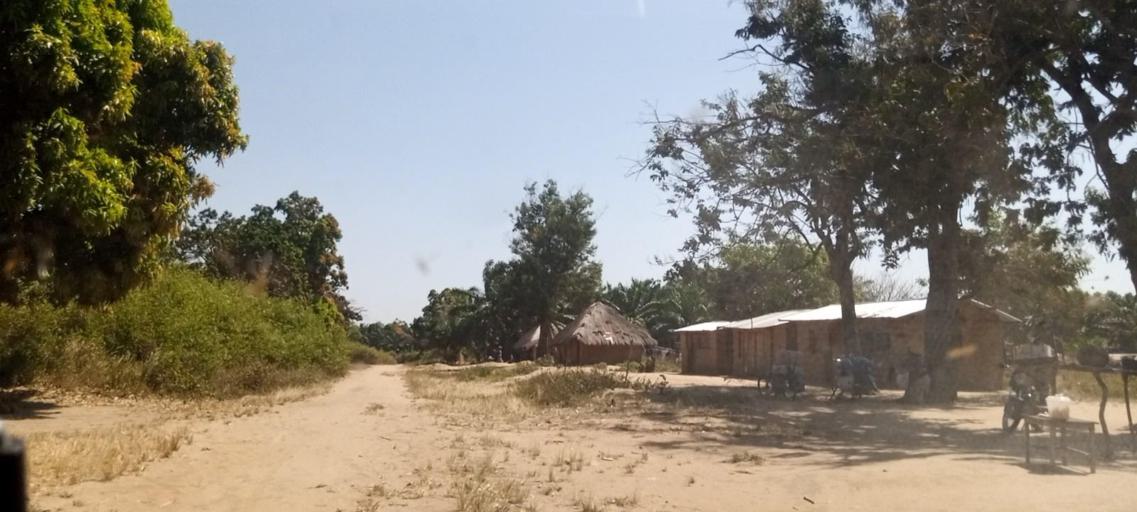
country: CD
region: Kasai-Oriental
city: Kabinda
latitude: -5.9613
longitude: 24.7763
